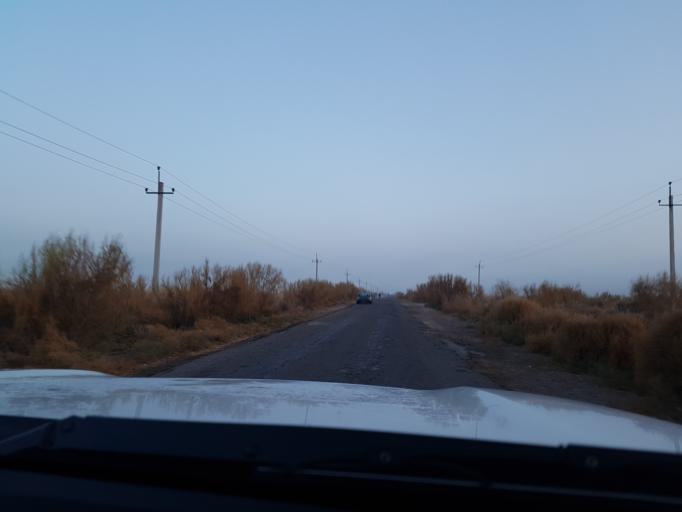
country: TM
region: Dasoguz
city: Koeneuergench
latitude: 41.7863
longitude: 58.6977
